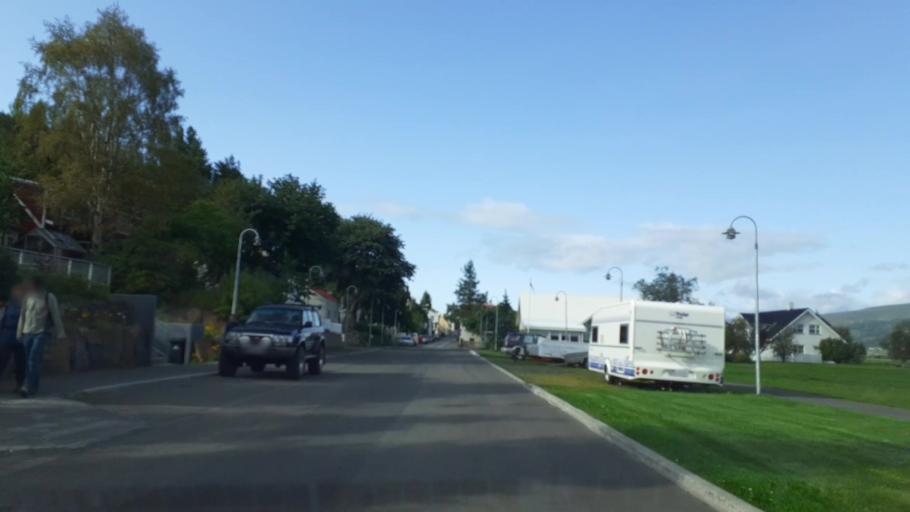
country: IS
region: Northeast
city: Akureyri
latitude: 65.6683
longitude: -18.0855
